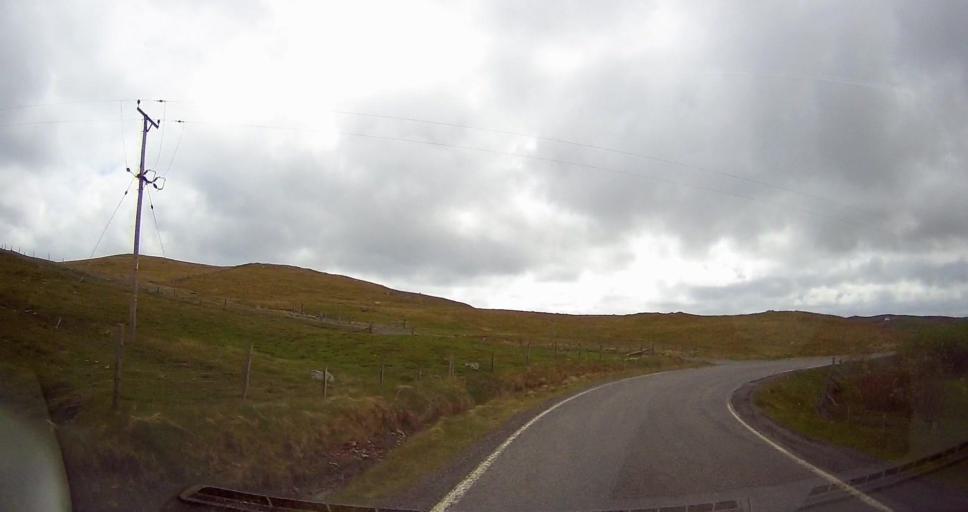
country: GB
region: Scotland
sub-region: Shetland Islands
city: Sandwick
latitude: 60.2335
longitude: -1.5522
